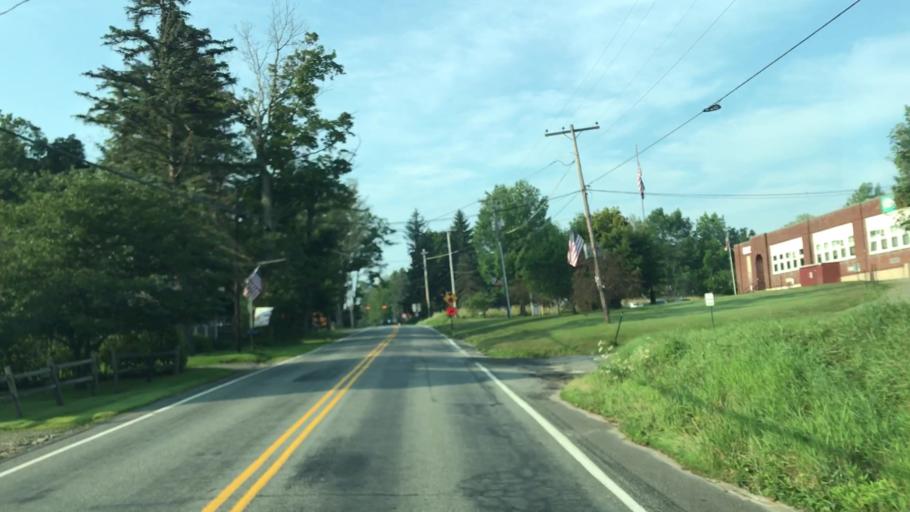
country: US
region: Pennsylvania
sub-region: Lackawanna County
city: Dalton
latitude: 41.6000
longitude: -75.7147
